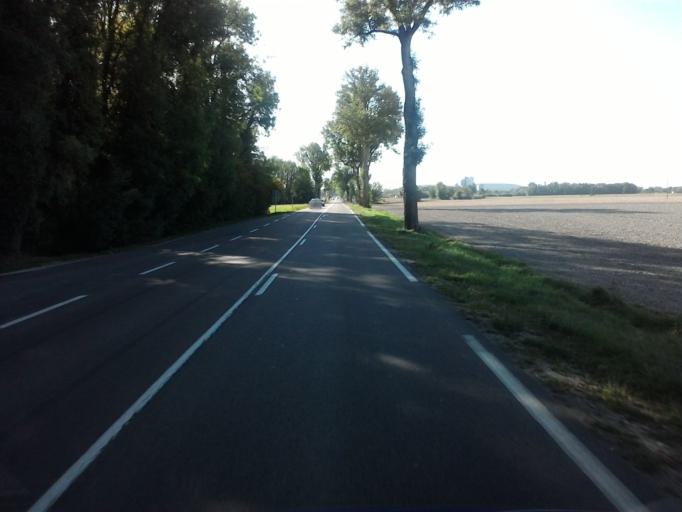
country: FR
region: Champagne-Ardenne
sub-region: Departement de l'Aube
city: Bar-sur-Seine
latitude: 48.0879
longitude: 4.3806
